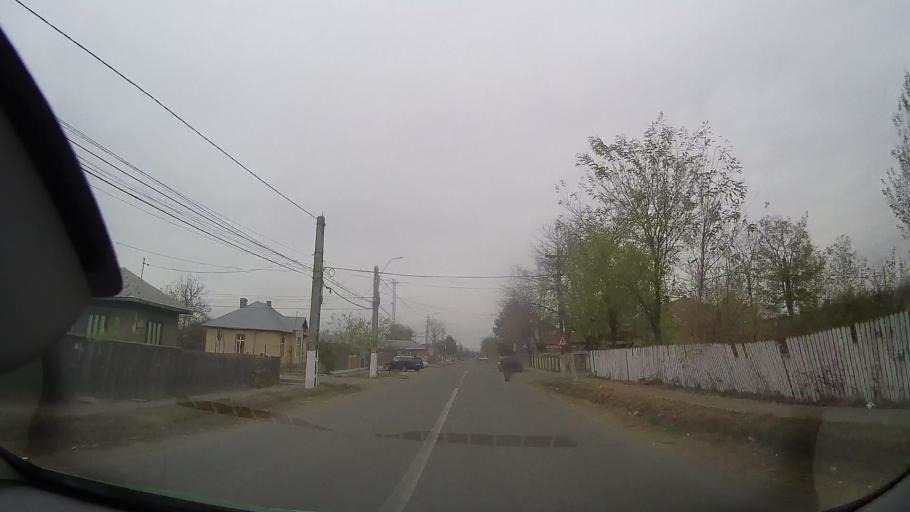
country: RO
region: Braila
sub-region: Comuna Budesti
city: Tataru
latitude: 44.8469
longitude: 27.4283
